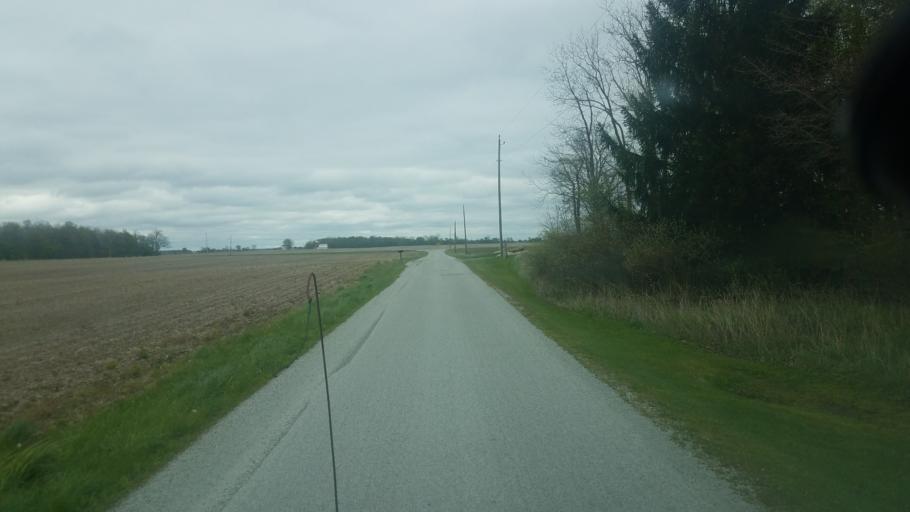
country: US
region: Ohio
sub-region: Hardin County
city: Kenton
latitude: 40.6800
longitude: -83.5410
